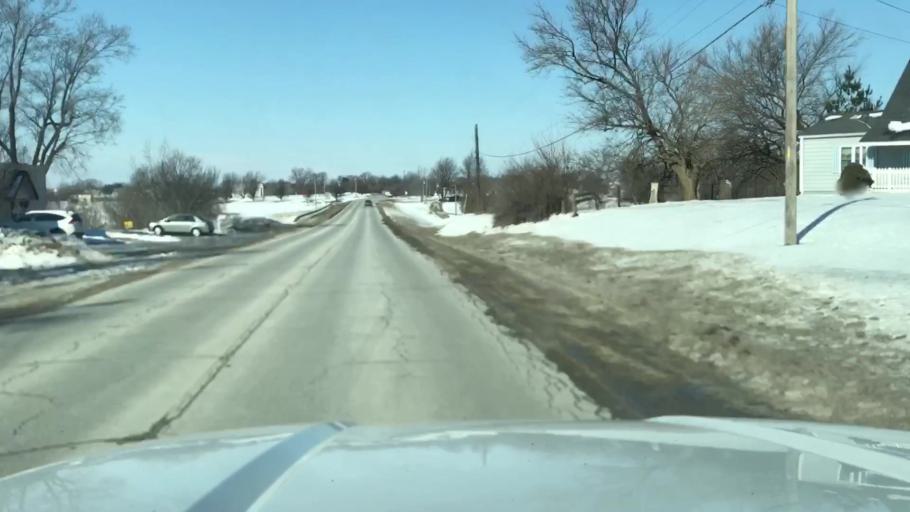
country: US
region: Missouri
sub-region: Andrew County
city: Savannah
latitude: 39.9485
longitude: -94.8417
